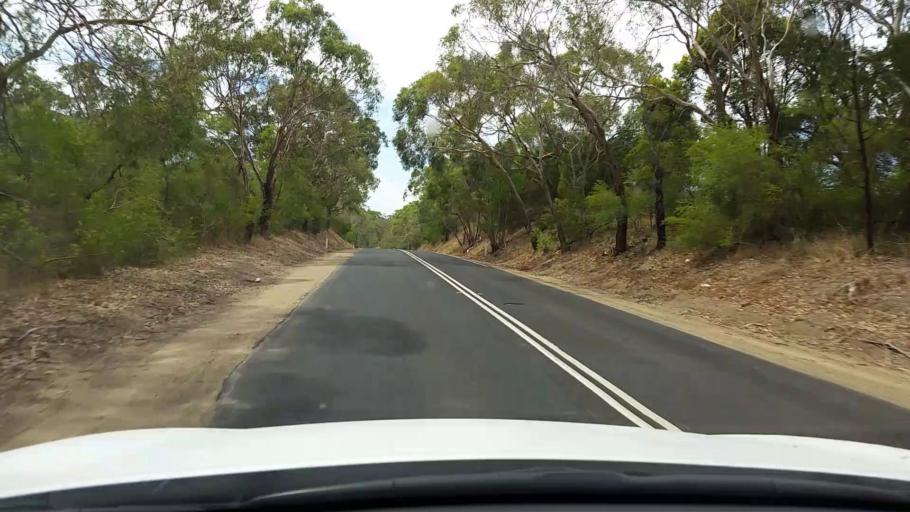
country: AU
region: Victoria
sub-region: Mornington Peninsula
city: Mount Martha
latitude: -38.2996
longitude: 145.0435
